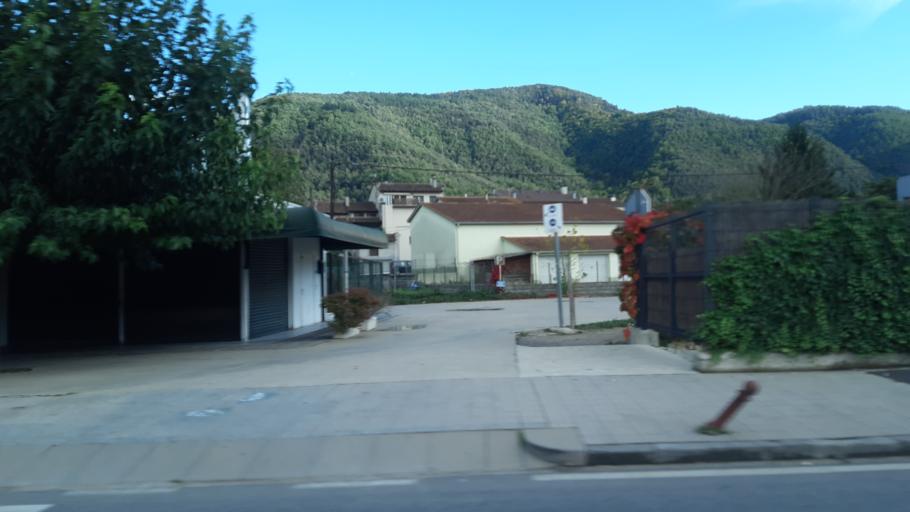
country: ES
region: Catalonia
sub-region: Provincia de Girona
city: Bas
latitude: 42.1443
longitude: 2.4585
